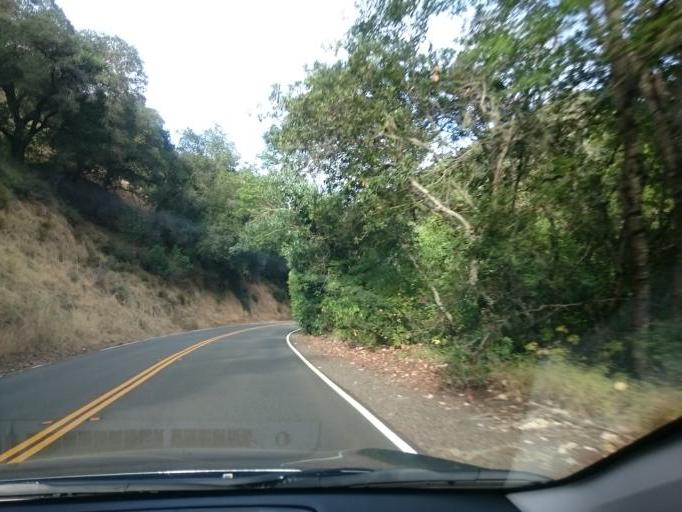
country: US
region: California
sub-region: Napa County
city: Yountville
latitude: 38.4868
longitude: -122.3147
